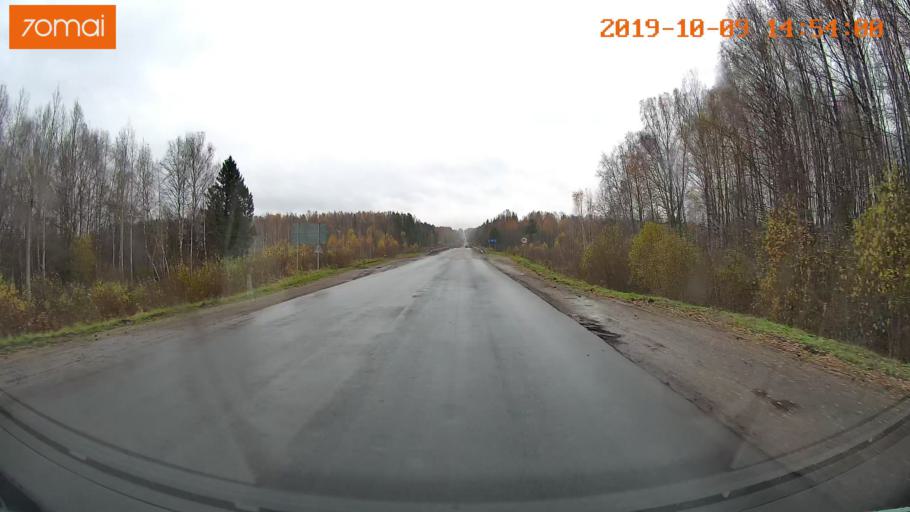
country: RU
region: Kostroma
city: Chistyye Bory
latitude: 58.3610
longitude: 41.6411
